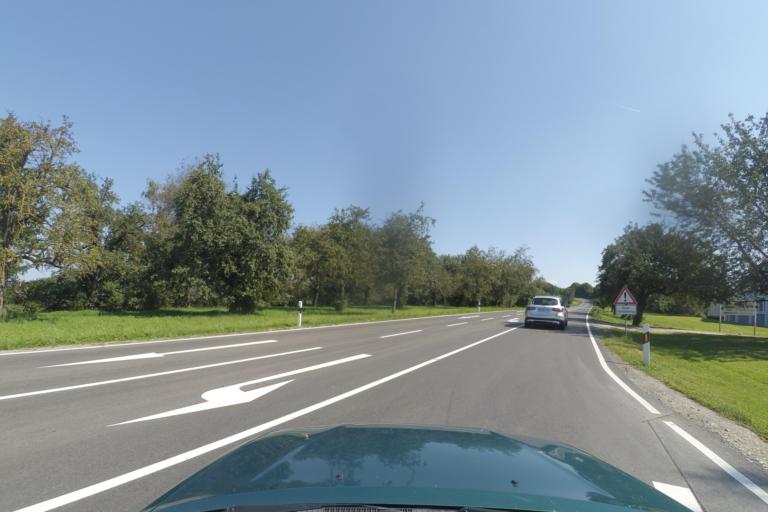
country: DE
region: Baden-Wuerttemberg
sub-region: Regierungsbezirk Stuttgart
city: Crailsheim
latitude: 49.1227
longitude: 10.0930
